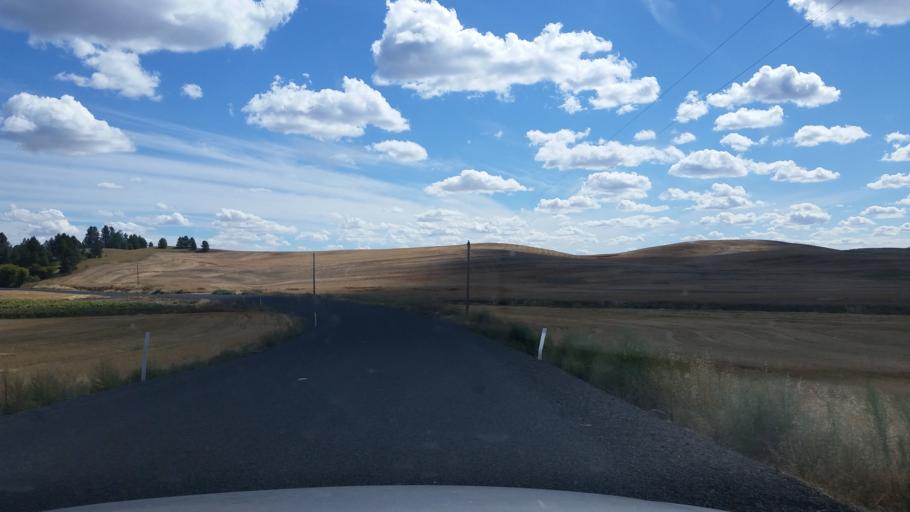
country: US
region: Washington
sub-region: Spokane County
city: Cheney
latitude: 47.4845
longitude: -117.6141
